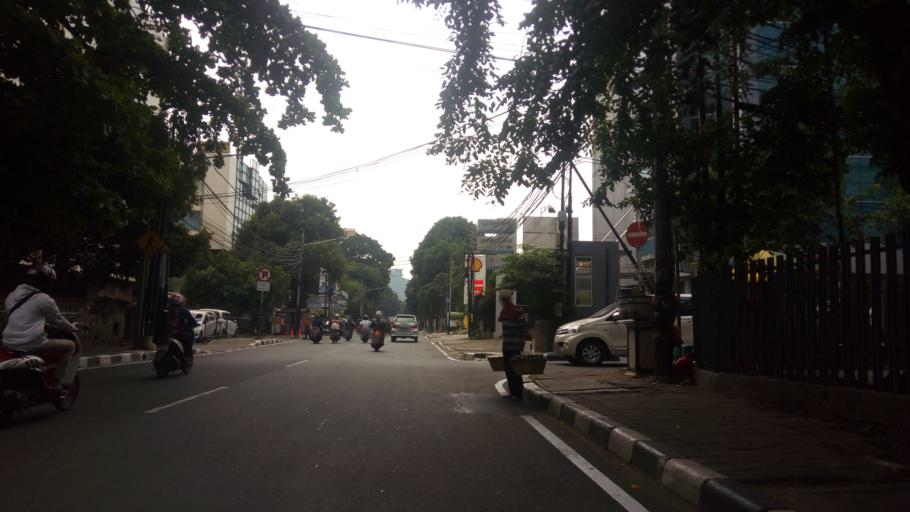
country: ID
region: Jakarta Raya
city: Jakarta
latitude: -6.1920
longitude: 106.8366
